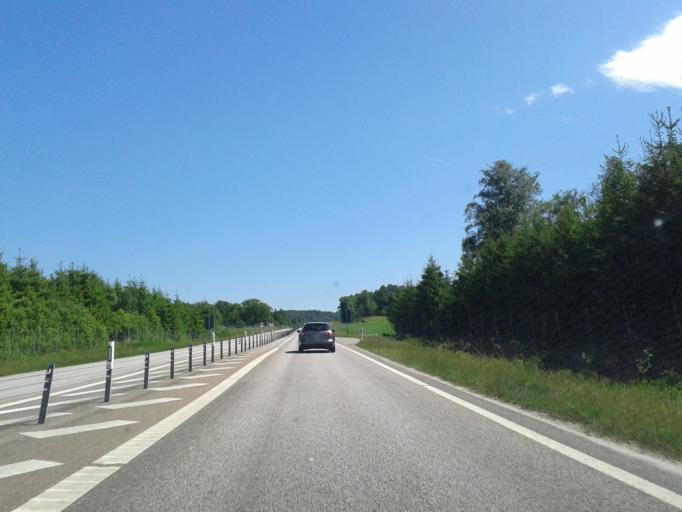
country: SE
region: Vaestra Goetaland
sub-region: Orust
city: Henan
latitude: 58.3504
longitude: 11.7225
